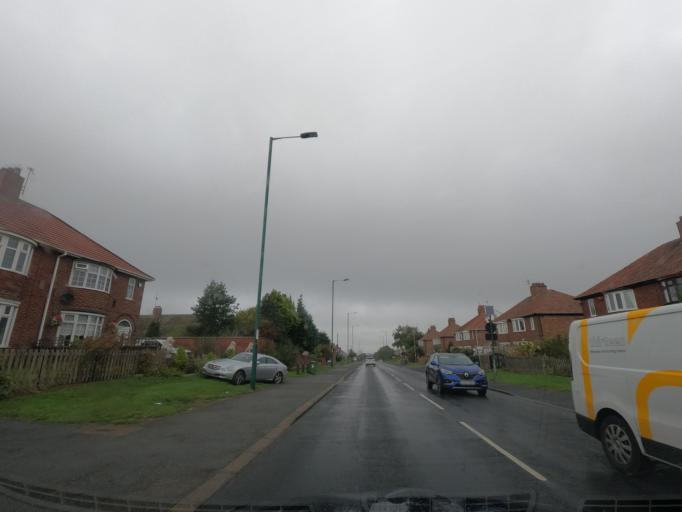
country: GB
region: England
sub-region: Middlesbrough
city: Nunthorpe
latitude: 54.5443
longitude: -1.1762
